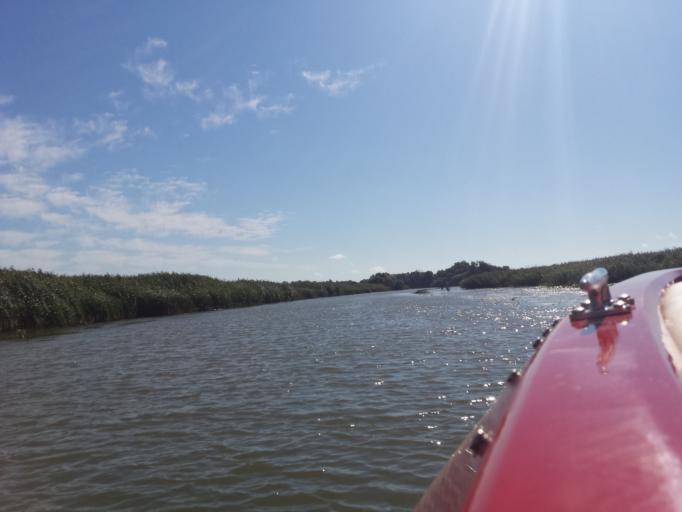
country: RO
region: Tulcea
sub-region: Comuna Pardina
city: Pardina
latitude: 45.2453
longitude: 29.0720
